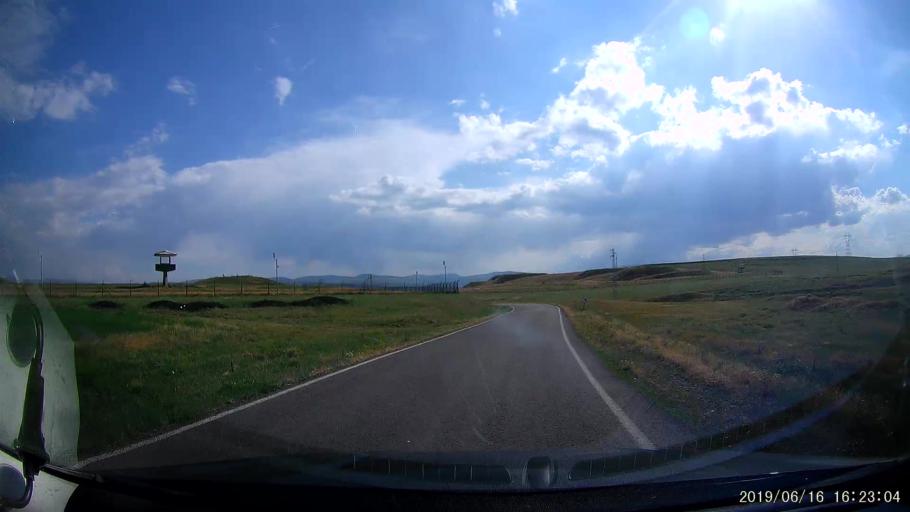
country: TR
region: Erzurum
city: Ilica
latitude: 39.9814
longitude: 41.1085
